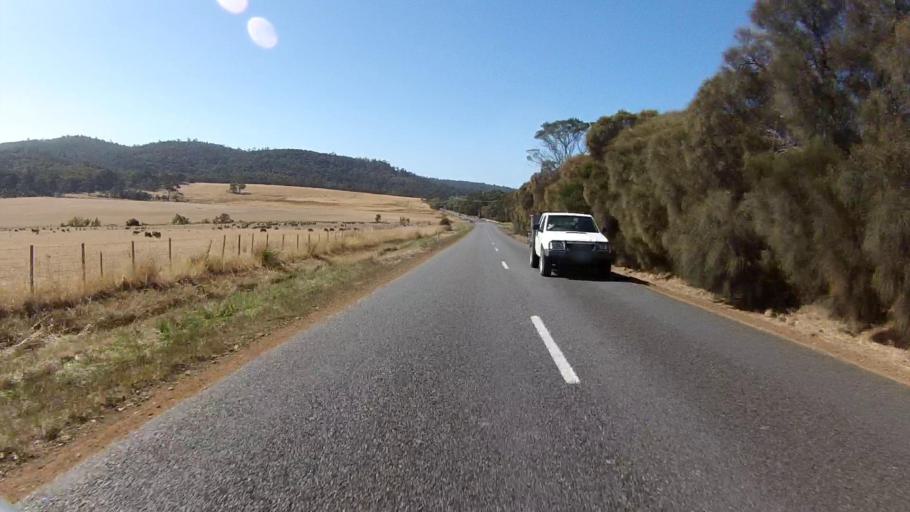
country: AU
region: Tasmania
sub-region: Sorell
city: Sorell
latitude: -42.2488
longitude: 148.0088
